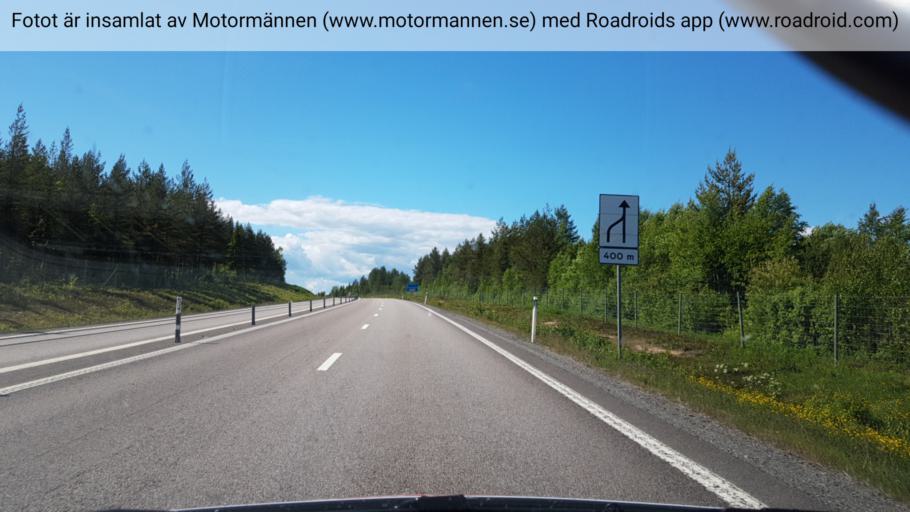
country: SE
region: Norrbotten
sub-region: Kalix Kommun
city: Toere
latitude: 65.9170
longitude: 22.7741
